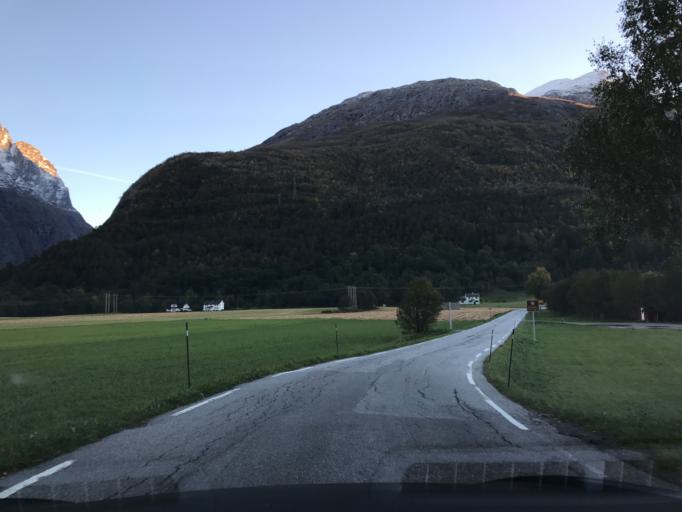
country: NO
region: More og Romsdal
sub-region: Rauma
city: Andalsnes
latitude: 62.5325
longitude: 7.7370
